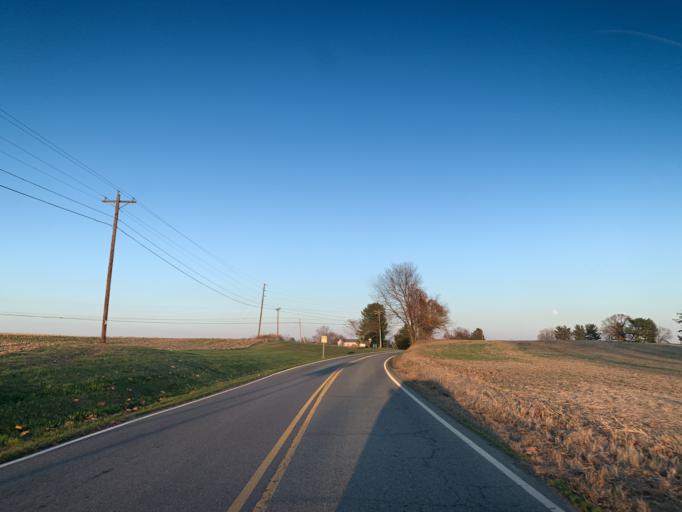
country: US
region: Maryland
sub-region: Cecil County
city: Charlestown
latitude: 39.4070
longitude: -75.9395
